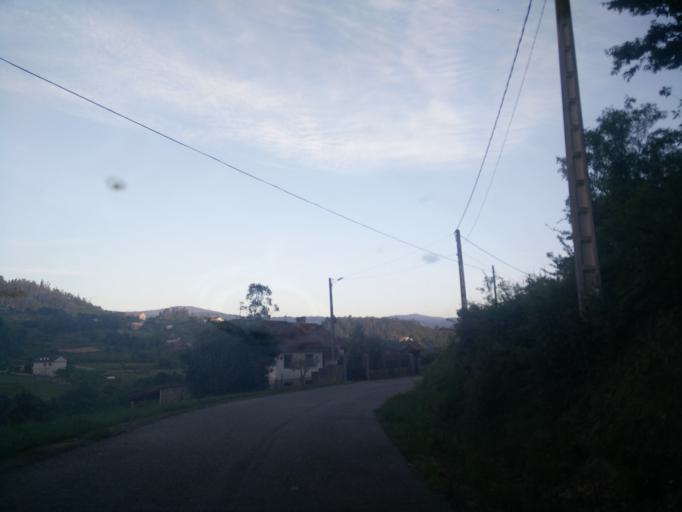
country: ES
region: Galicia
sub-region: Provincia de Pontevedra
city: Mondariz
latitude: 42.2686
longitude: -8.4080
